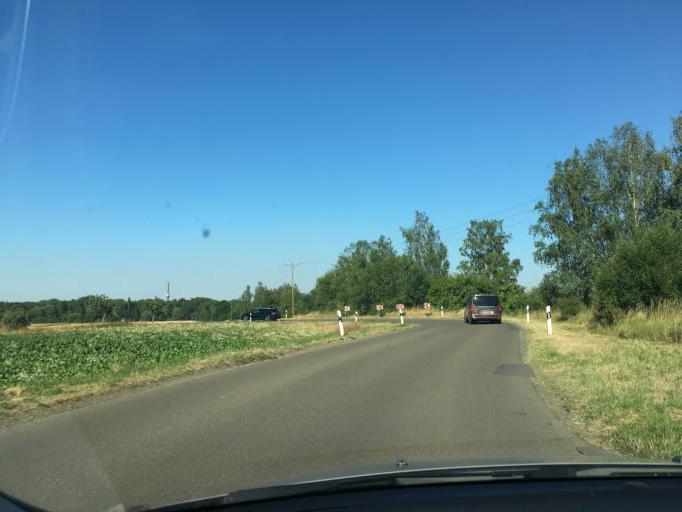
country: DE
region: Saxony
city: Borna
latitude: 51.0839
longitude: 12.5095
